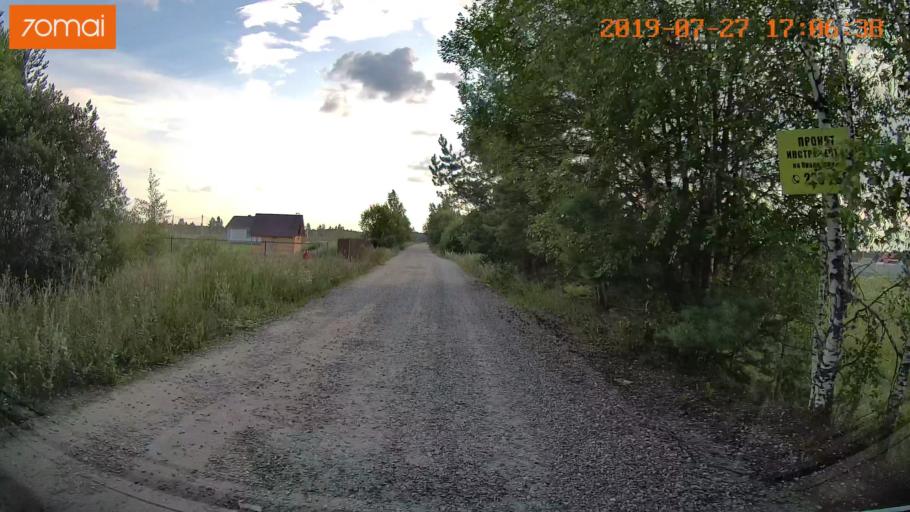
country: RU
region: Ivanovo
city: Novo-Talitsy
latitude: 57.0864
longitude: 40.8407
